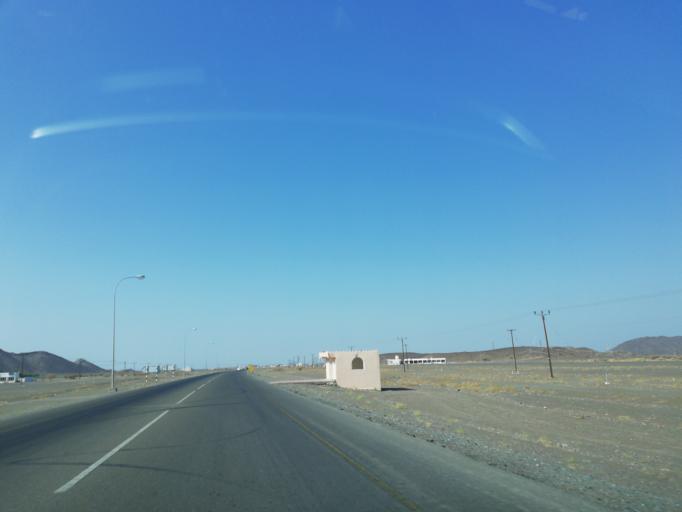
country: OM
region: Ash Sharqiyah
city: Ibra'
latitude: 22.7202
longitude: 58.1482
